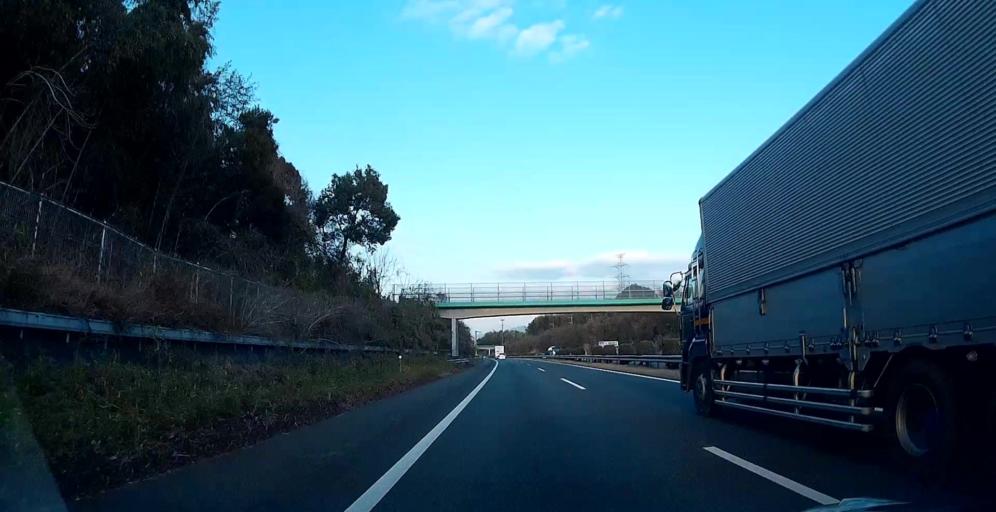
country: JP
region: Kumamoto
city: Uto
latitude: 32.6796
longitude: 130.7285
